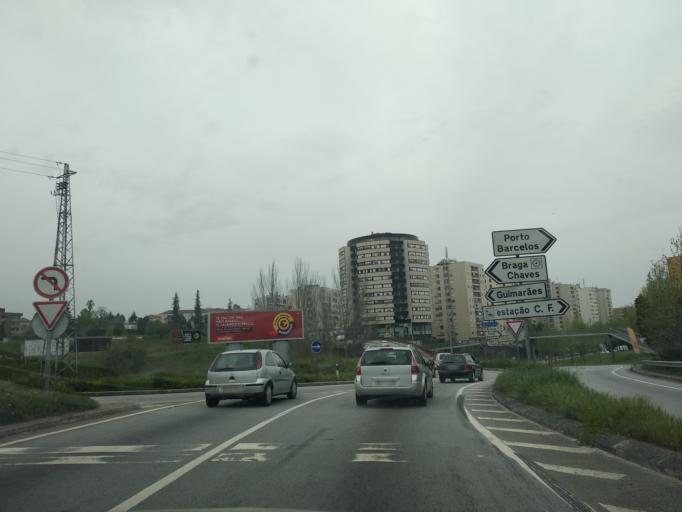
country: PT
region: Braga
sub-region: Braga
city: Braga
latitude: 41.5619
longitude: -8.4188
